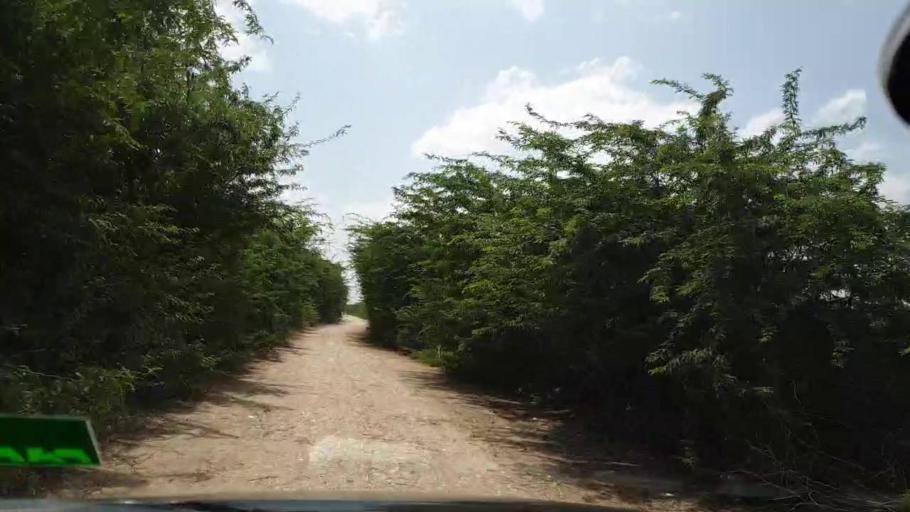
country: PK
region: Sindh
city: Kadhan
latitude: 24.5563
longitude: 69.2113
